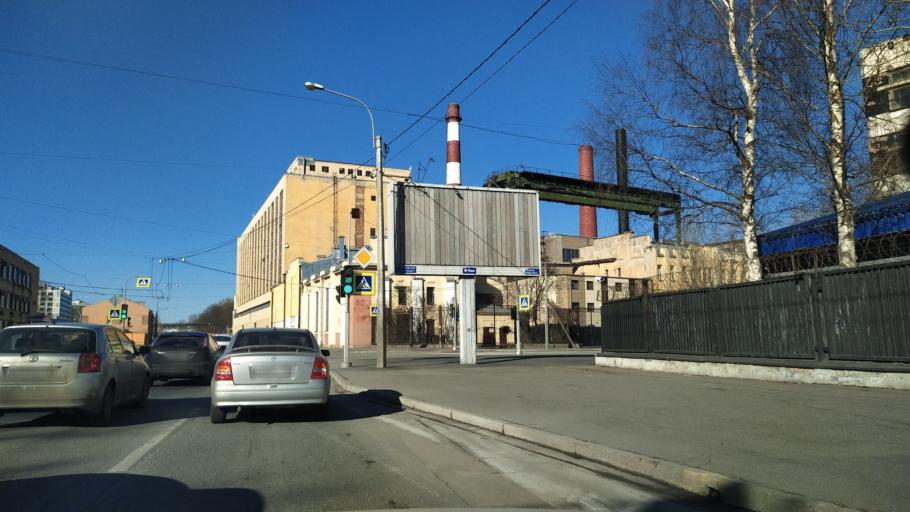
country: RU
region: St.-Petersburg
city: Centralniy
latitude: 59.9164
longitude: 30.3748
